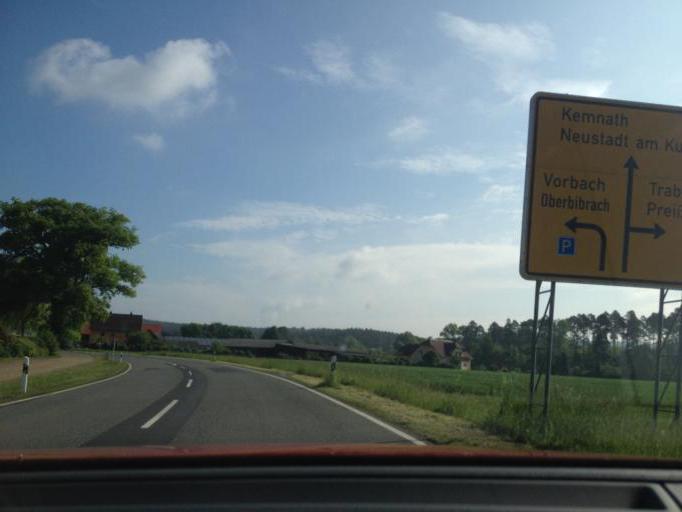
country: DE
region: Bavaria
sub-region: Upper Palatinate
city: Speinshart
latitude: 49.7854
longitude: 11.8217
